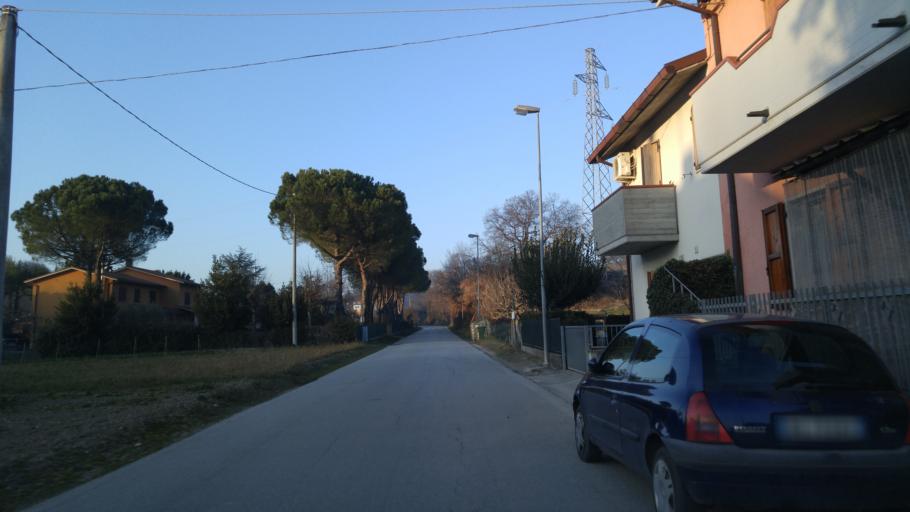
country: IT
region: The Marches
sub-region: Provincia di Pesaro e Urbino
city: Fenile
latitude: 43.8473
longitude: 12.9681
